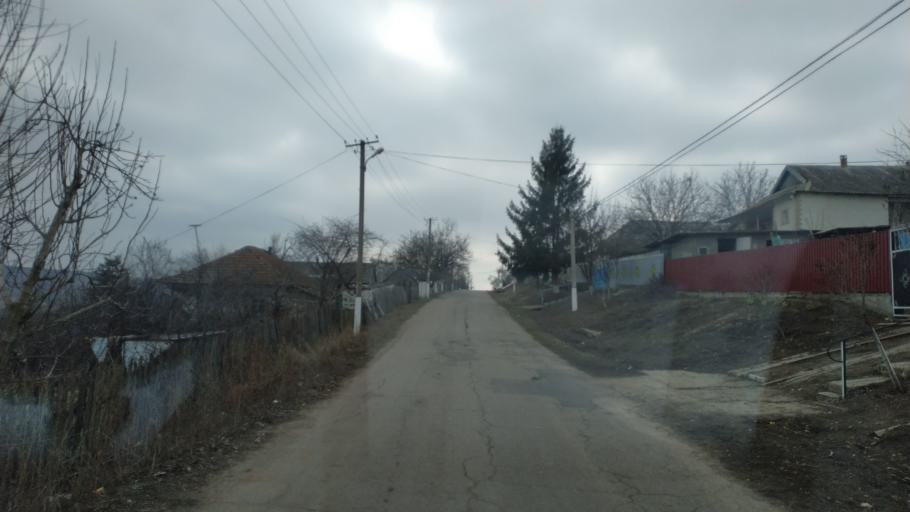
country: MD
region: Hincesti
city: Dancu
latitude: 46.8880
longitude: 28.3225
